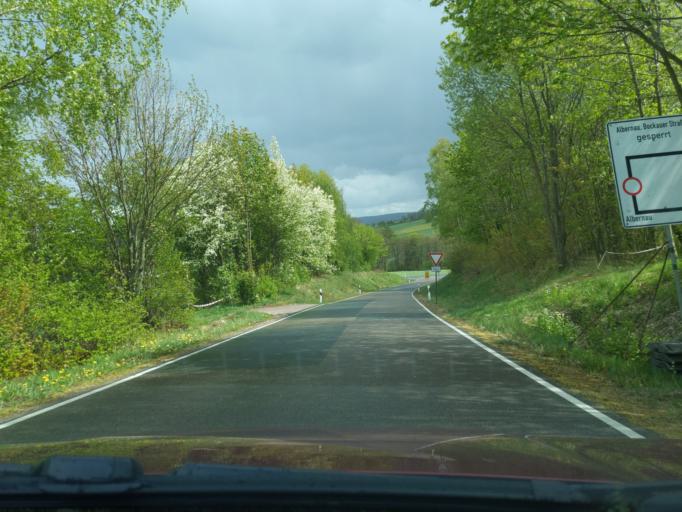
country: DE
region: Saxony
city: Zschorlau
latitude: 50.5578
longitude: 12.6272
